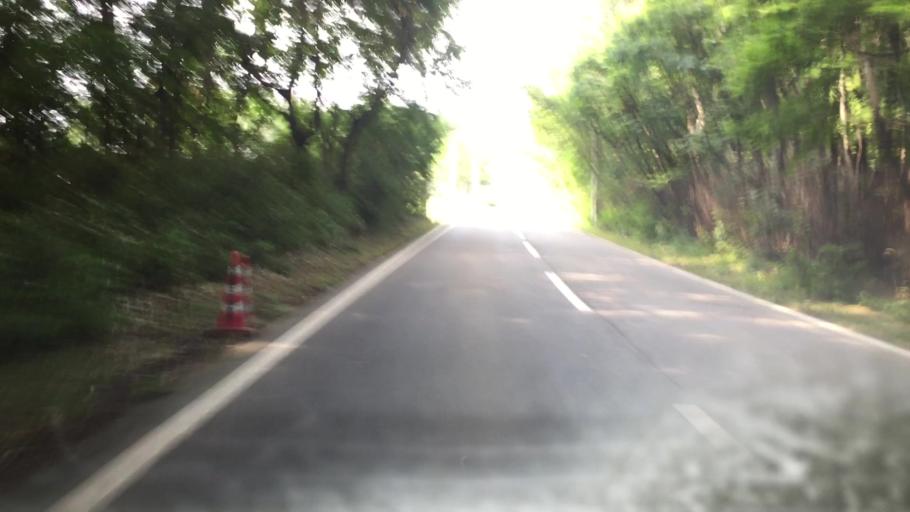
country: JP
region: Tochigi
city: Kuroiso
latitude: 36.9462
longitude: 139.9601
